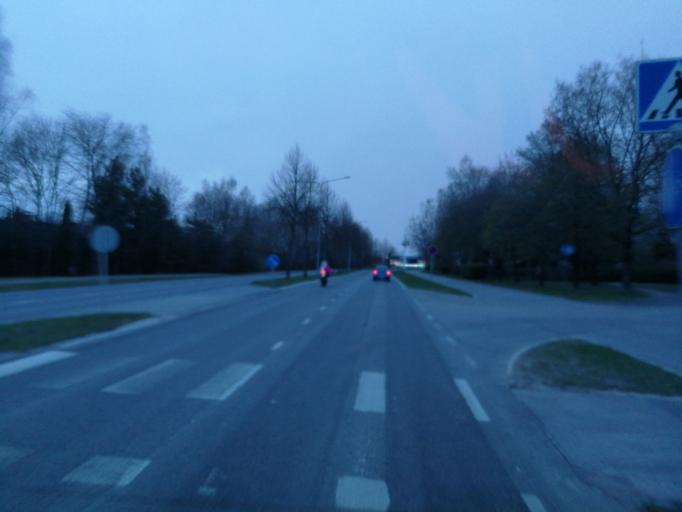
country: FI
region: Varsinais-Suomi
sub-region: Turku
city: Turku
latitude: 60.4647
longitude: 22.2541
